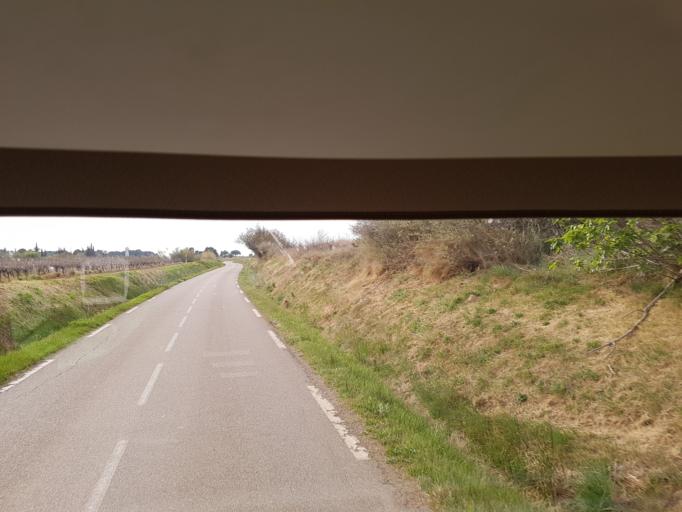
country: FR
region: Languedoc-Roussillon
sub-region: Departement de l'Herault
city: Marseillan
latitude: 43.3661
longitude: 3.5129
